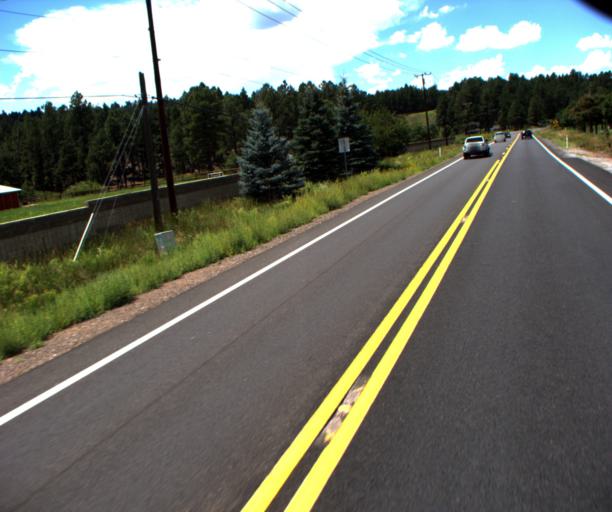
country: US
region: Arizona
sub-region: Coconino County
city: Flagstaff
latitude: 35.2396
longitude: -111.6779
